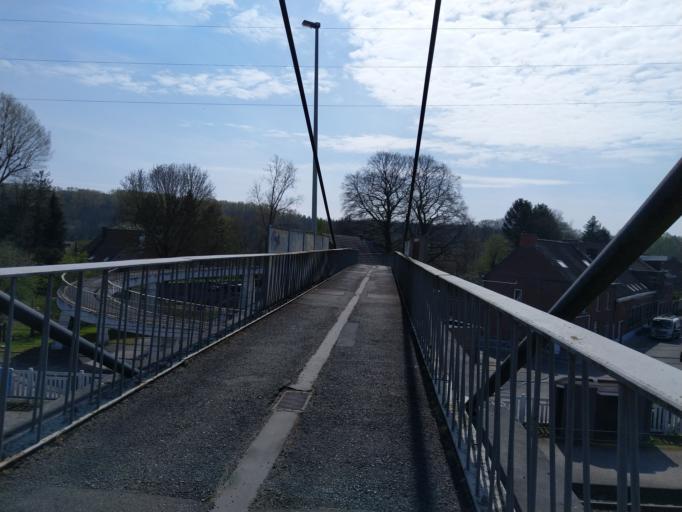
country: BE
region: Wallonia
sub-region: Province du Hainaut
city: Mons
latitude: 50.4700
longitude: 4.0077
